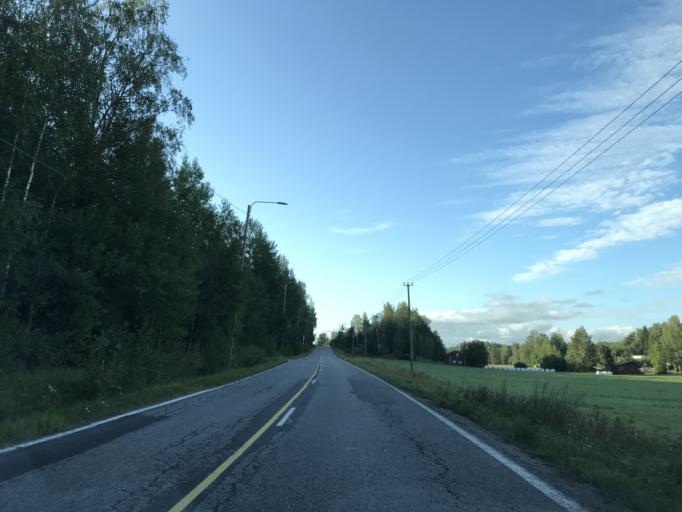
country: FI
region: Uusimaa
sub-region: Helsinki
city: Kauniainen
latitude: 60.3641
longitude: 24.6834
